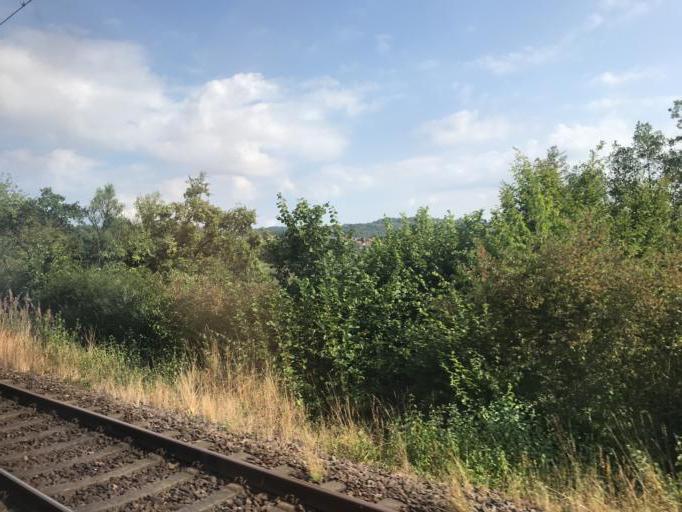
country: DE
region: Saarland
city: Neunkirchen
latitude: 49.3642
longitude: 7.1734
